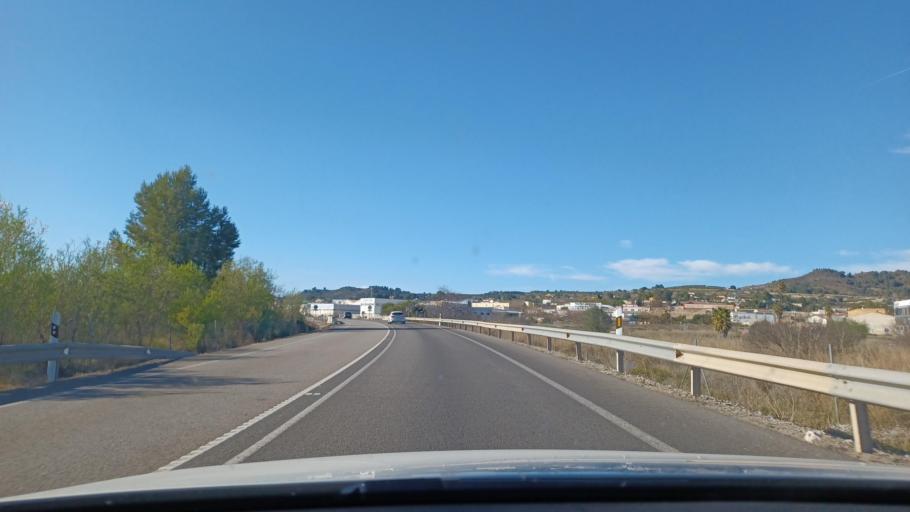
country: ES
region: Valencia
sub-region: Provincia de Valencia
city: Llosa de Ranes
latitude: 39.0127
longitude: -0.5348
